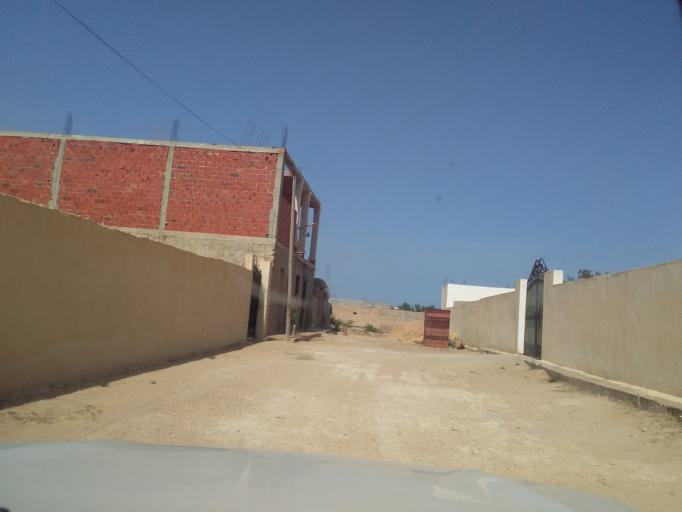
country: TN
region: Qabis
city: Gabes
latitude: 33.6322
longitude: 10.2855
